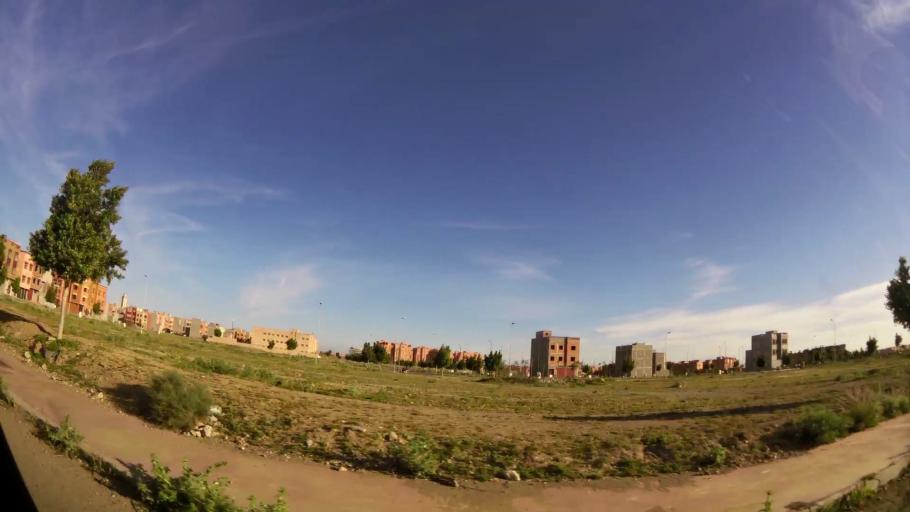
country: MA
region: Marrakech-Tensift-Al Haouz
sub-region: Marrakech
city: Marrakesh
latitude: 31.7610
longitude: -8.1045
